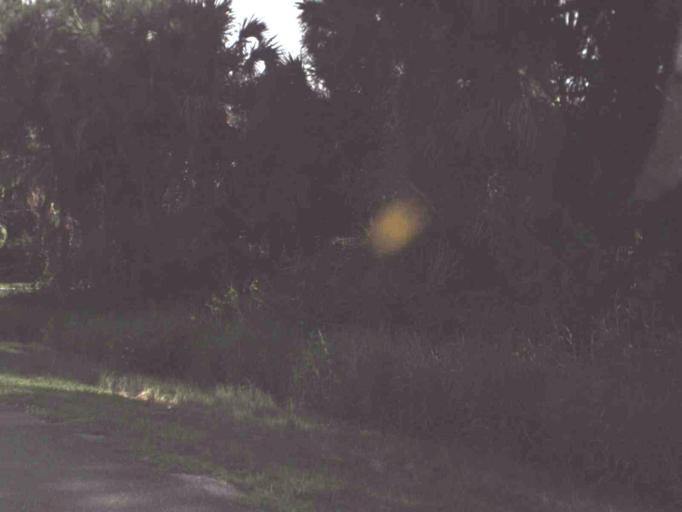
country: US
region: Florida
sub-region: Charlotte County
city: Cleveland
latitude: 26.9634
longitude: -81.7607
